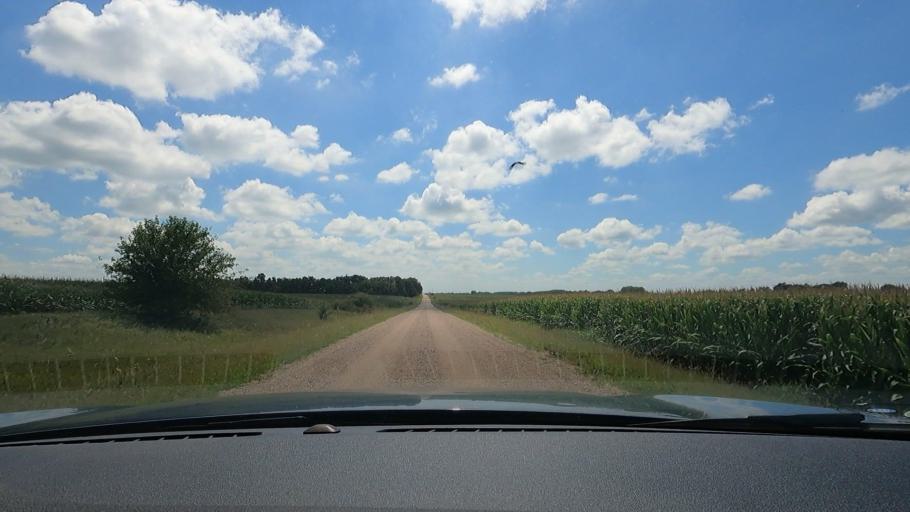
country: US
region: Nebraska
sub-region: Saunders County
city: Wahoo
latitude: 41.2690
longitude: -96.5419
